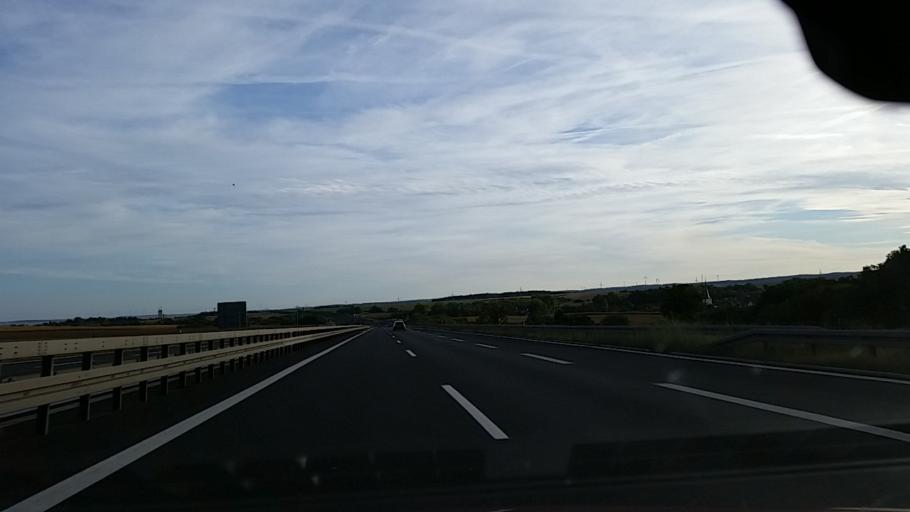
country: DE
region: Bavaria
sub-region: Regierungsbezirk Unterfranken
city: Poppenhausen
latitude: 50.0887
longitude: 10.1555
